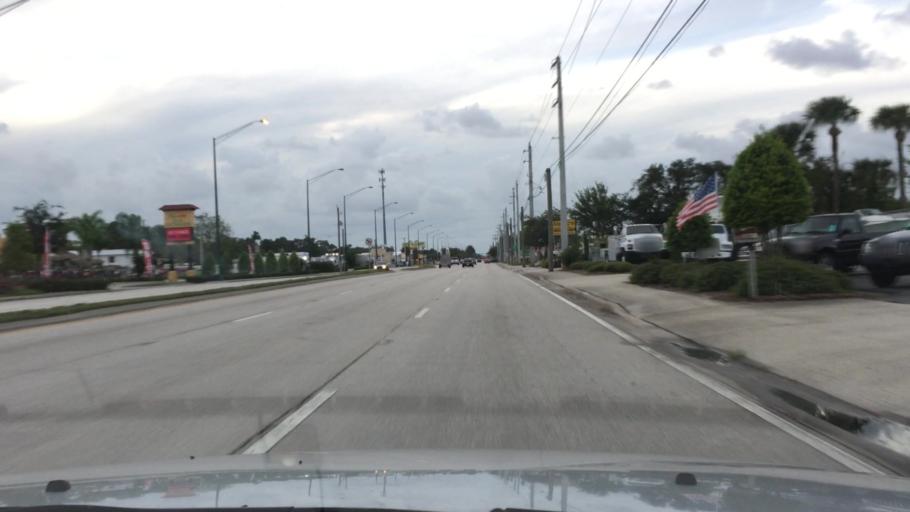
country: US
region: Florida
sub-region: Volusia County
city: Holly Hill
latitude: 29.2539
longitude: -81.0716
